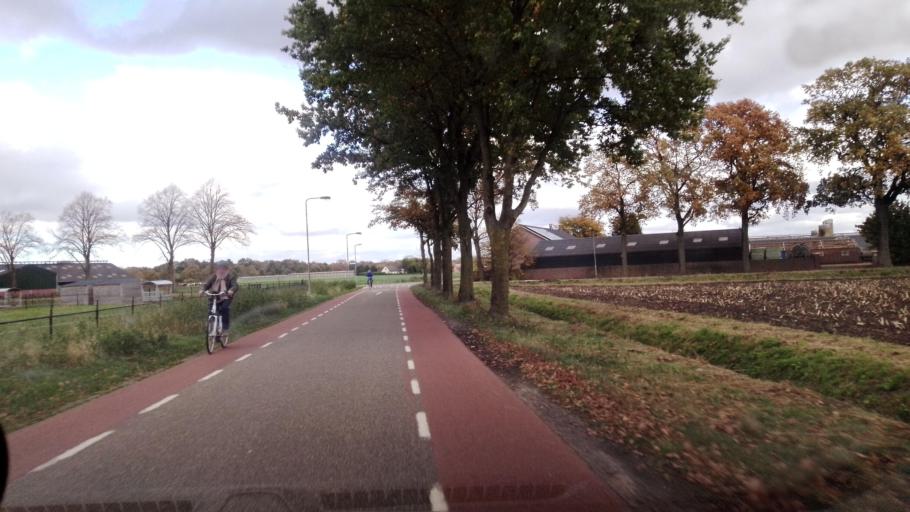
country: NL
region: Limburg
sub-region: Gemeente Venray
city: Venray
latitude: 51.5071
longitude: 5.9532
